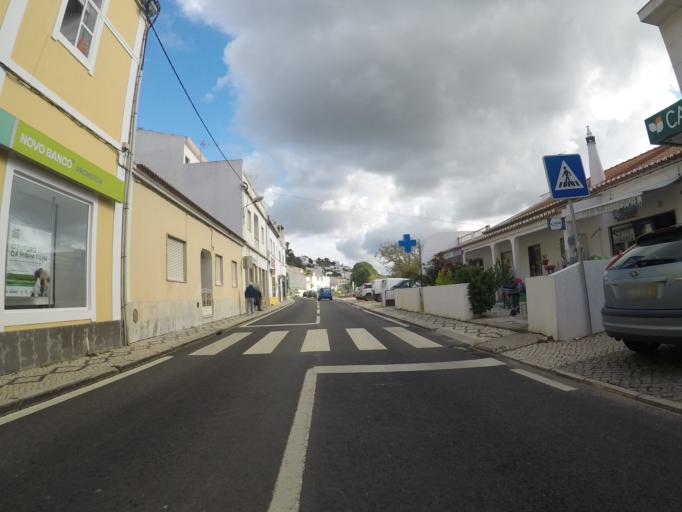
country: PT
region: Faro
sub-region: Aljezur
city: Aljezur
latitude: 37.3150
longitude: -8.8037
